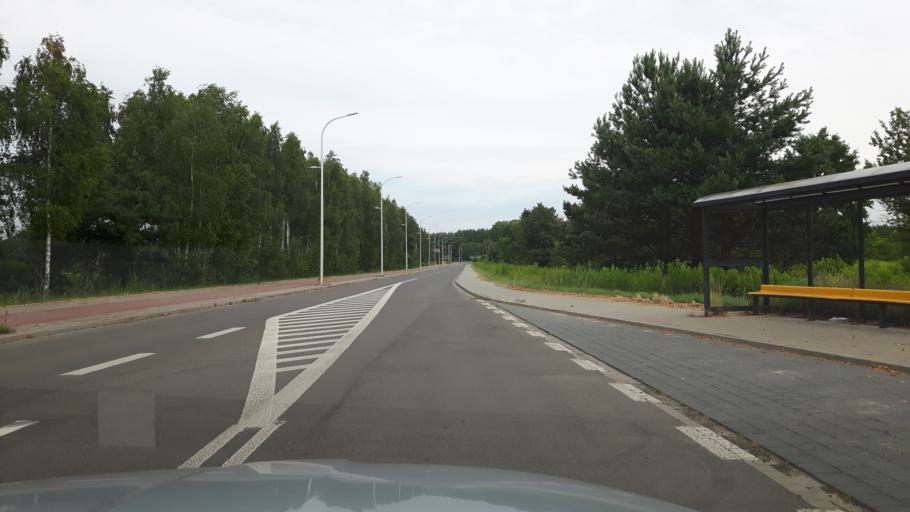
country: PL
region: Masovian Voivodeship
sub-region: Powiat wolominski
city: Wolomin
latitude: 52.3156
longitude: 21.2197
